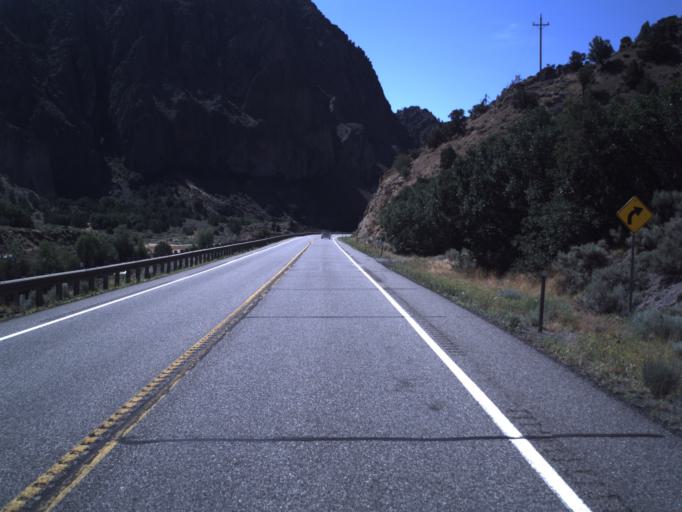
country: US
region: Utah
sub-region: Sevier County
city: Monroe
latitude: 38.5526
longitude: -112.2702
